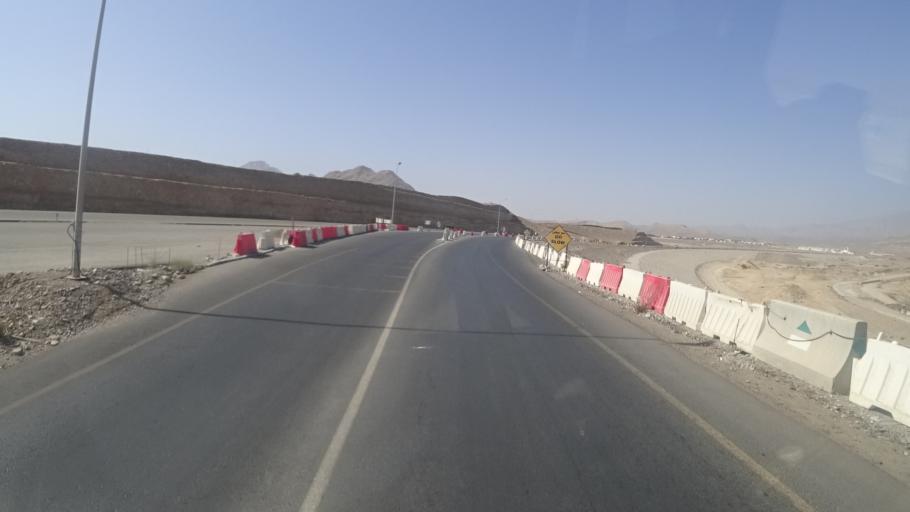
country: OM
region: Ash Sharqiyah
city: Sur
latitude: 22.5213
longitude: 59.4634
